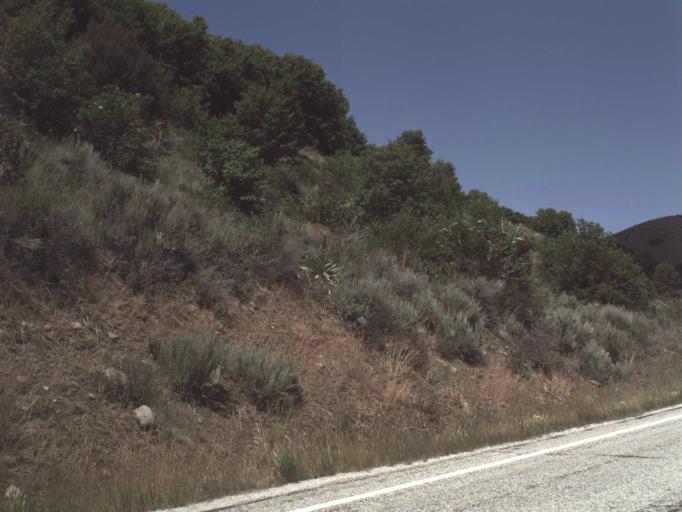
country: US
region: Utah
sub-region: Weber County
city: Wolf Creek
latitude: 41.3327
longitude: -111.6090
